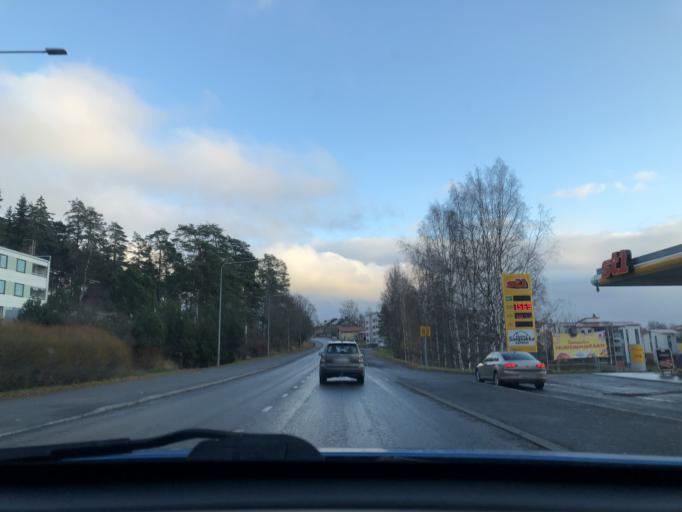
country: FI
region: Pirkanmaa
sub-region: Tampere
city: Kangasala
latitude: 61.4652
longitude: 24.0564
